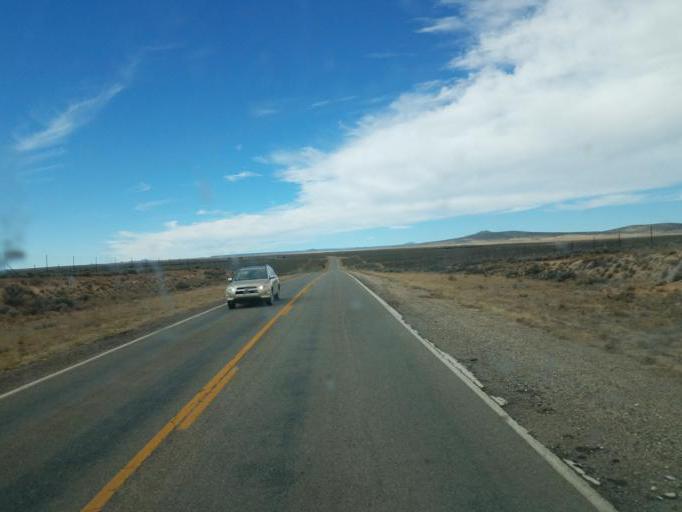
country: US
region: New Mexico
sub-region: Taos County
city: Arroyo Seco
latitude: 36.4745
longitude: -105.7156
